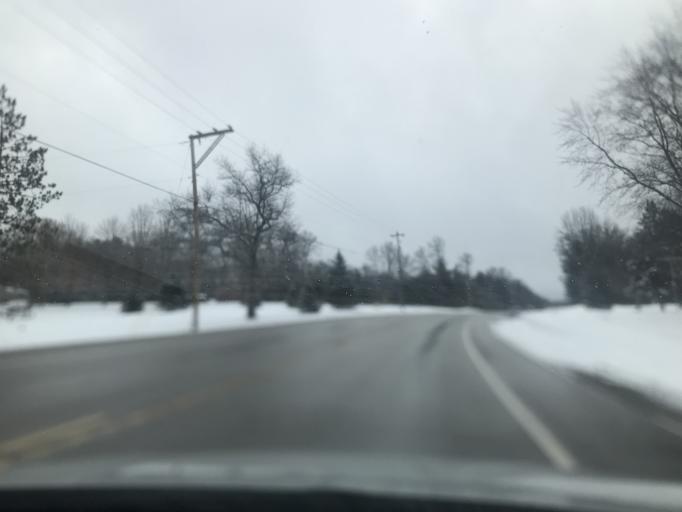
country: US
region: Wisconsin
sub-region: Marinette County
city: Peshtigo
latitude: 45.1682
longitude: -87.7311
